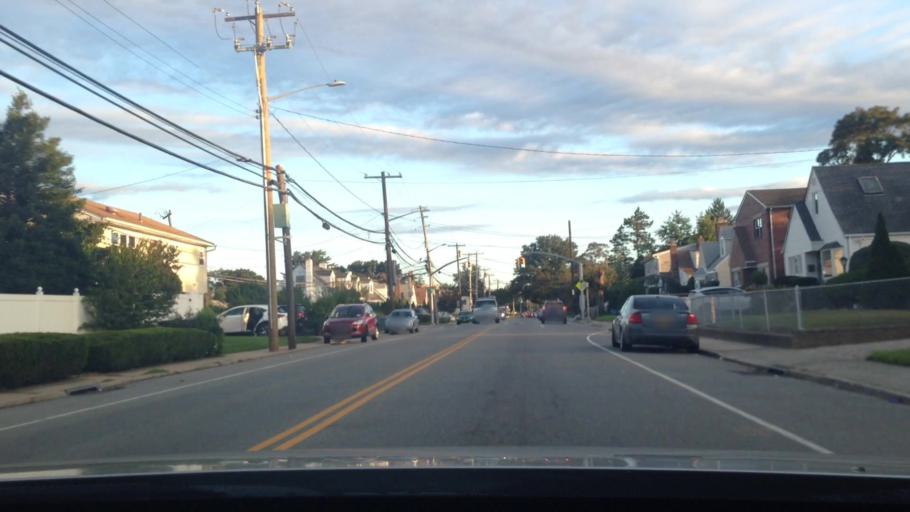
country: US
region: New York
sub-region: Nassau County
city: Garden City South
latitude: 40.7021
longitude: -73.6610
